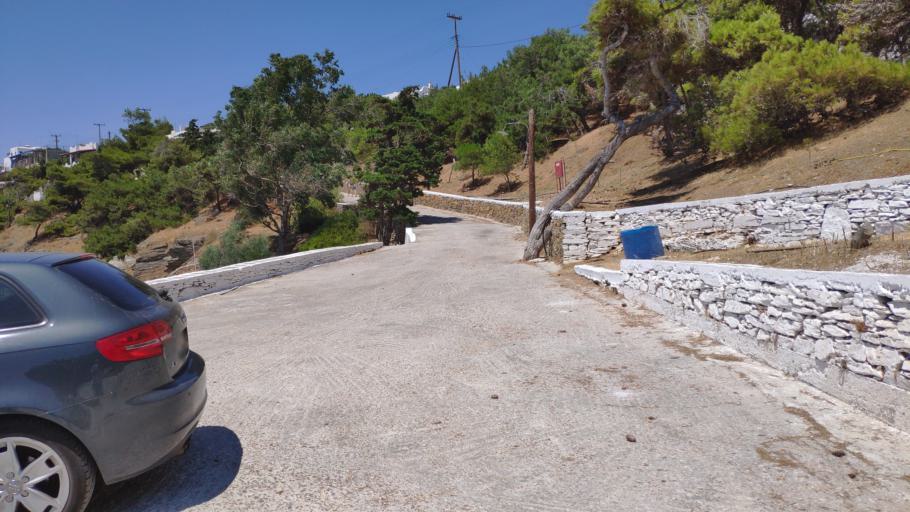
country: GR
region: South Aegean
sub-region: Nomos Kykladon
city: Kythnos
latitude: 37.3454
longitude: 24.4359
